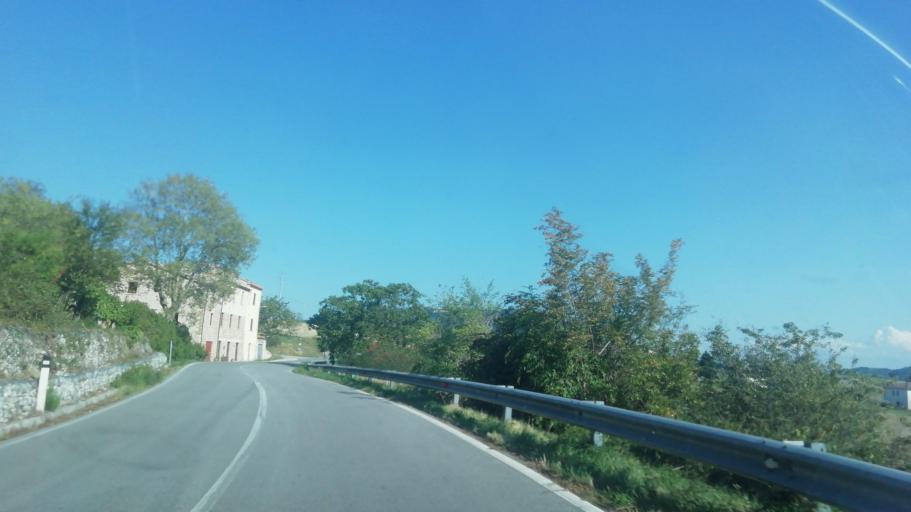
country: IT
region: The Marches
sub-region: Provincia di Pesaro e Urbino
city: Frontone
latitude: 43.5383
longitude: 12.7338
